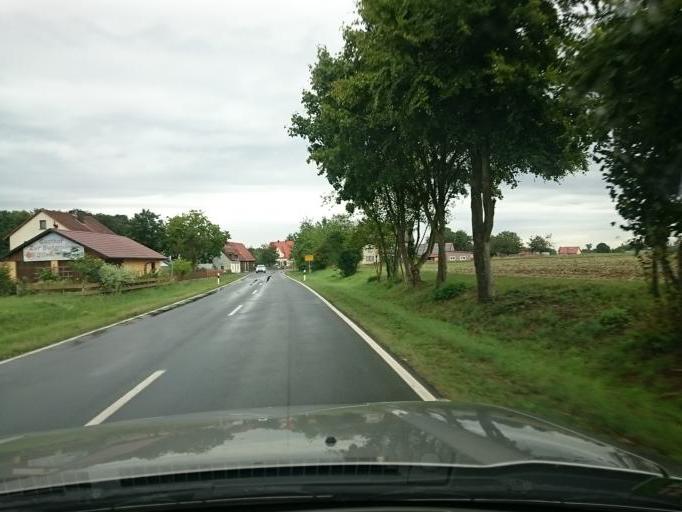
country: DE
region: Bavaria
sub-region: Upper Franconia
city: Obertrubach
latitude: 49.7085
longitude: 11.3890
